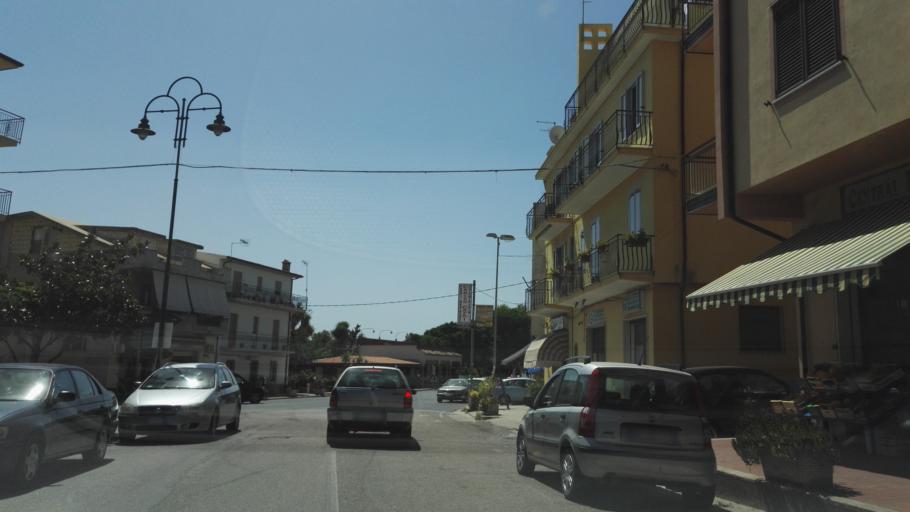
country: IT
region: Calabria
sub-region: Provincia di Catanzaro
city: Guardavalle Marina
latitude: 38.4822
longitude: 16.5781
